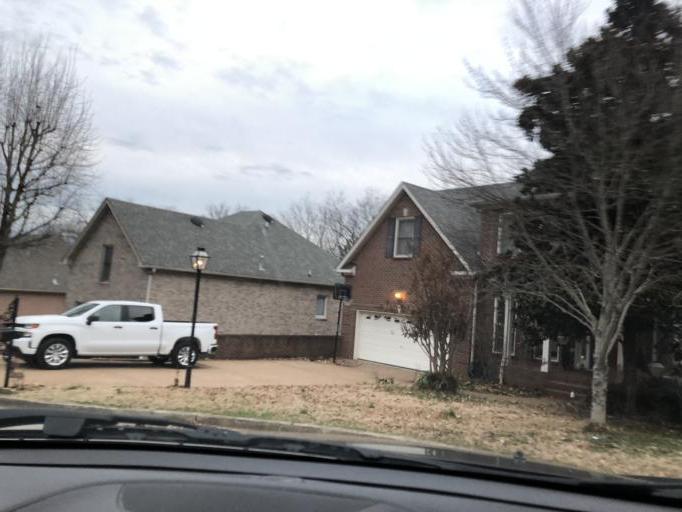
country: US
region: Tennessee
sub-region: Wilson County
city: Green Hill
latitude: 36.1970
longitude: -86.5922
